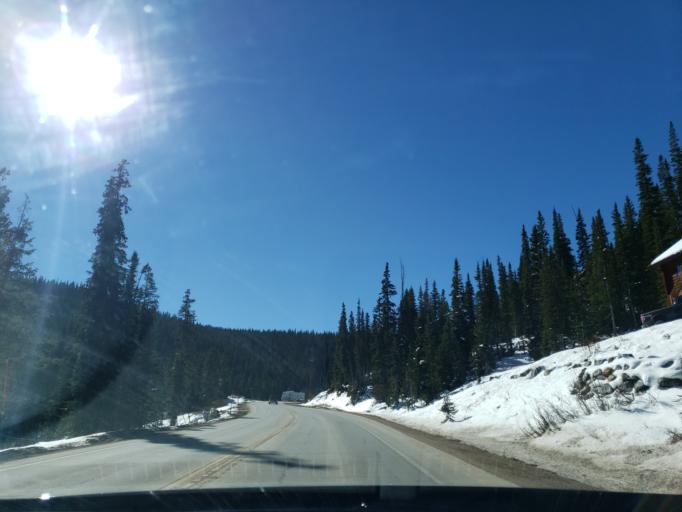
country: US
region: Colorado
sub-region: Summit County
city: Breckenridge
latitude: 39.3742
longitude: -106.0574
